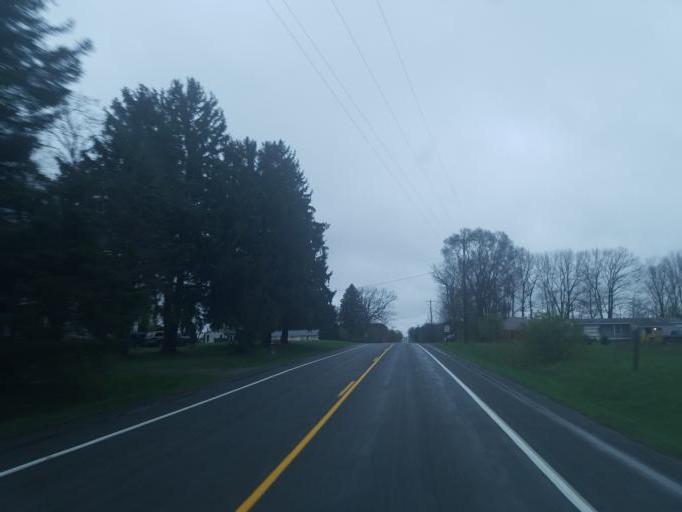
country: US
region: Michigan
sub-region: Montcalm County
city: Edmore
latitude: 43.4284
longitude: -85.0442
